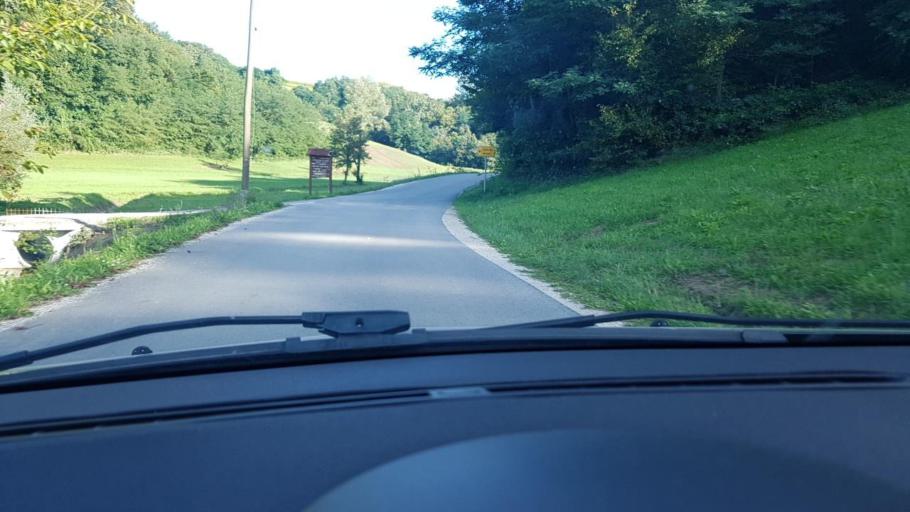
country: HR
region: Krapinsko-Zagorska
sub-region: Grad Krapina
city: Krapina
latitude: 46.1349
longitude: 15.8392
